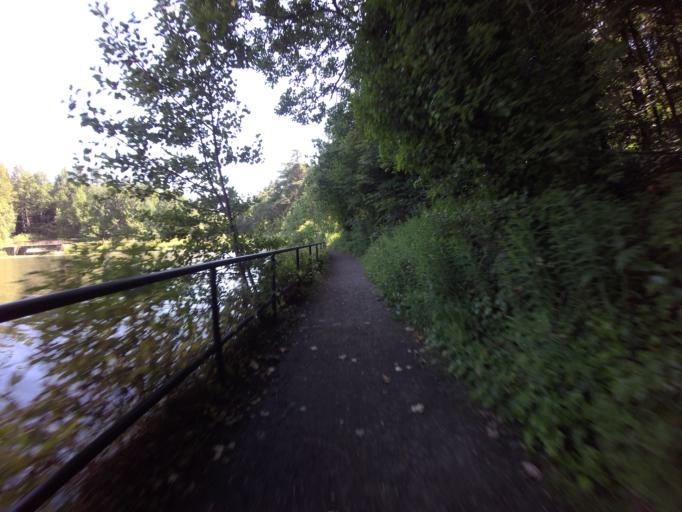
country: GB
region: Scotland
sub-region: West Lothian
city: Livingston
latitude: 55.8935
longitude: -3.5511
